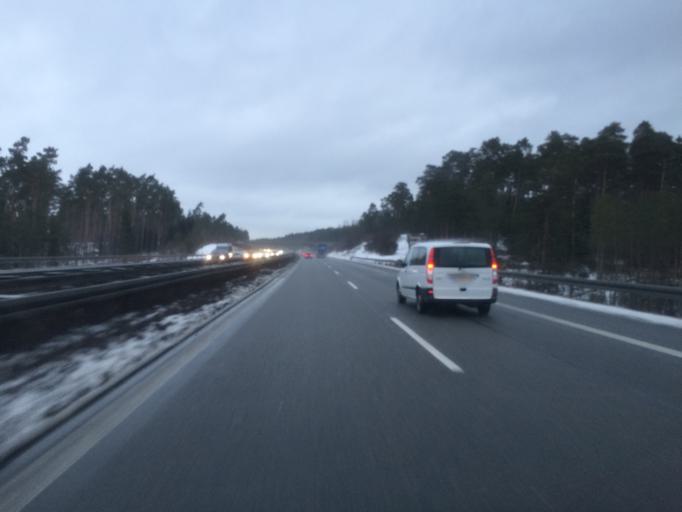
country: DE
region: Bavaria
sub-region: Upper Palatinate
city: Teublitz
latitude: 49.2293
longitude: 12.1314
